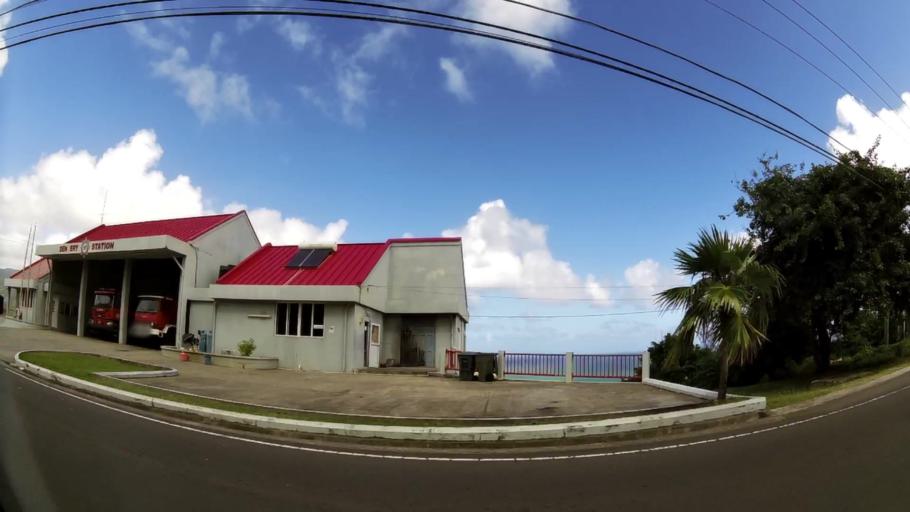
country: LC
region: Dennery Quarter
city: Dennery
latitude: 13.9178
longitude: -60.8928
